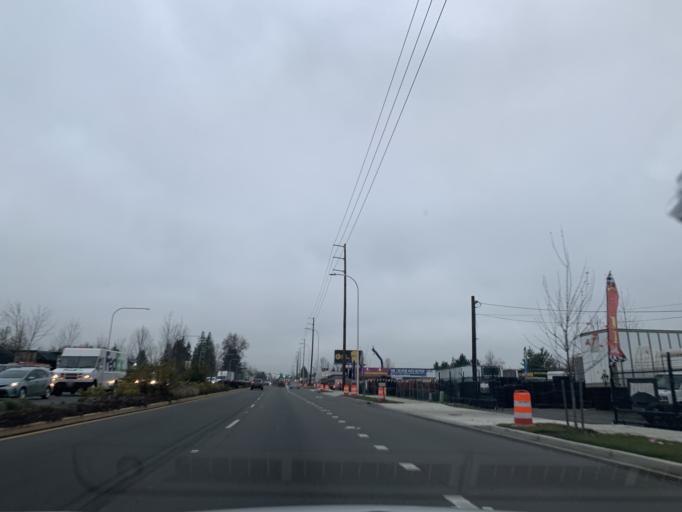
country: US
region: Washington
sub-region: Pierce County
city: Fife Heights
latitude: 47.2834
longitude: -122.3215
